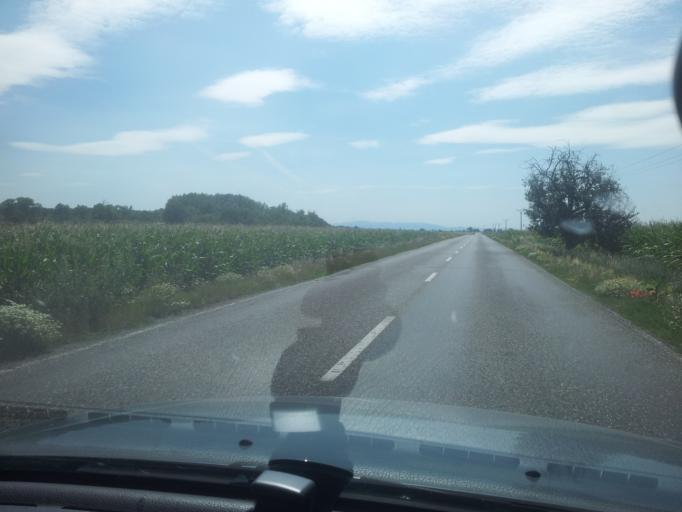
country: SK
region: Nitriansky
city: Levice
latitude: 48.1796
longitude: 18.5273
